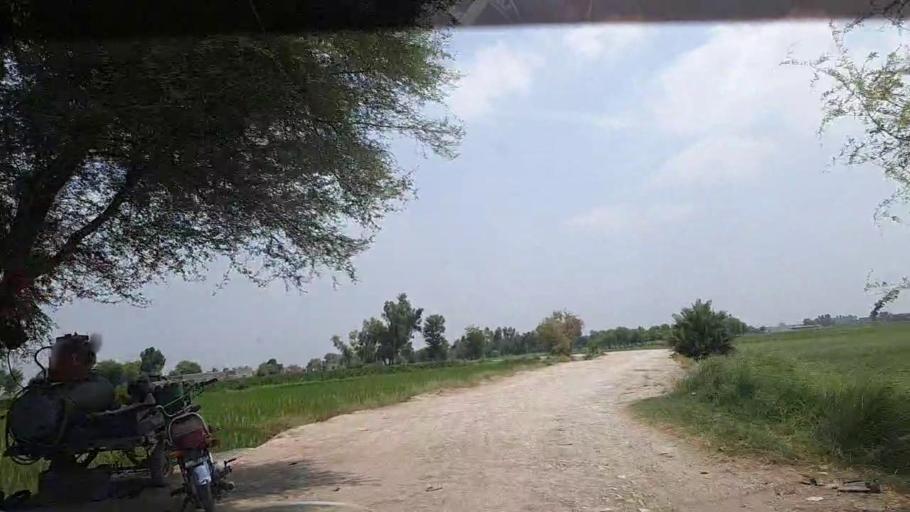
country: PK
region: Sindh
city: Khanpur
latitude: 27.8994
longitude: 69.3924
